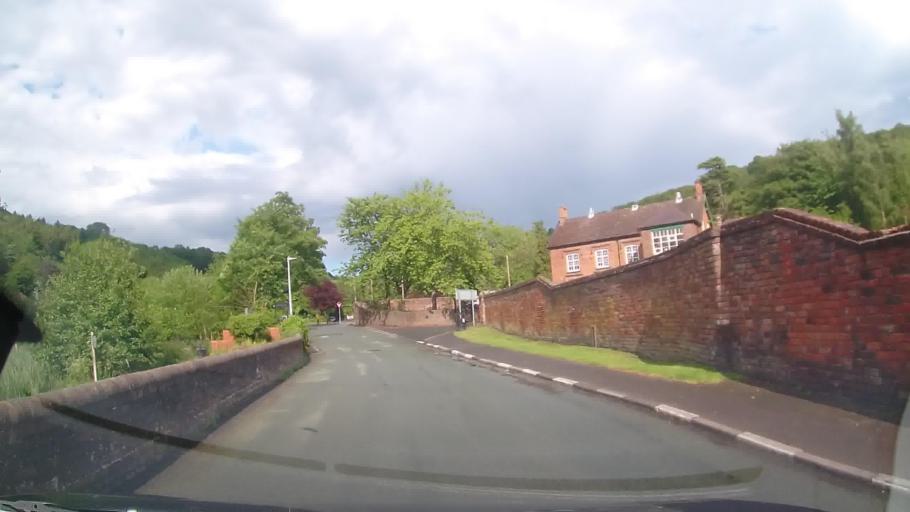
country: GB
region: England
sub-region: Telford and Wrekin
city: Ironbridge
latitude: 52.6406
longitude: -2.4927
